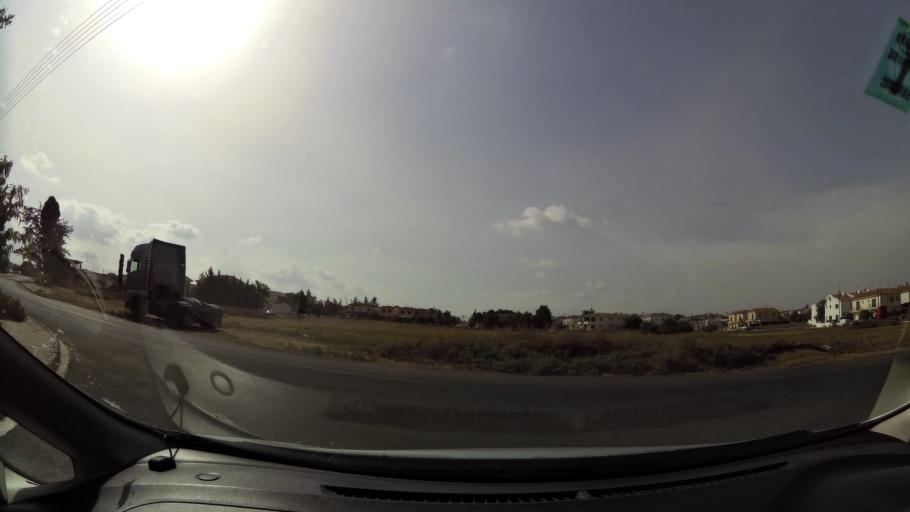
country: CY
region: Lefkosia
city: Geri
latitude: 35.0690
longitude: 33.3986
